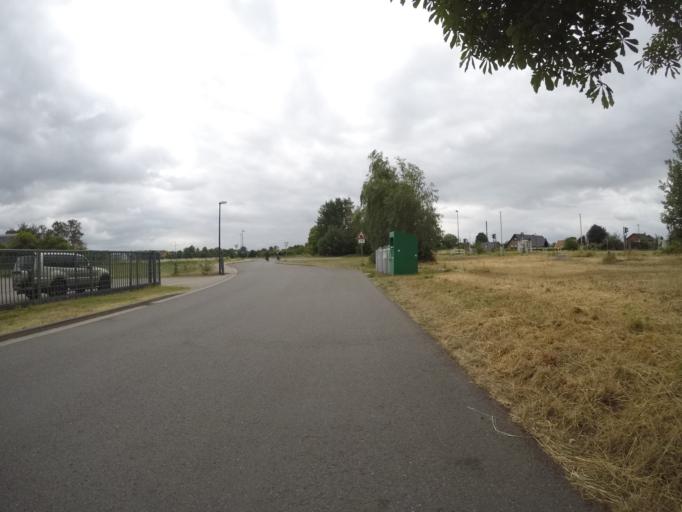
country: DE
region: North Rhine-Westphalia
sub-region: Regierungsbezirk Dusseldorf
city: Hamminkeln
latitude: 51.7676
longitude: 6.6084
